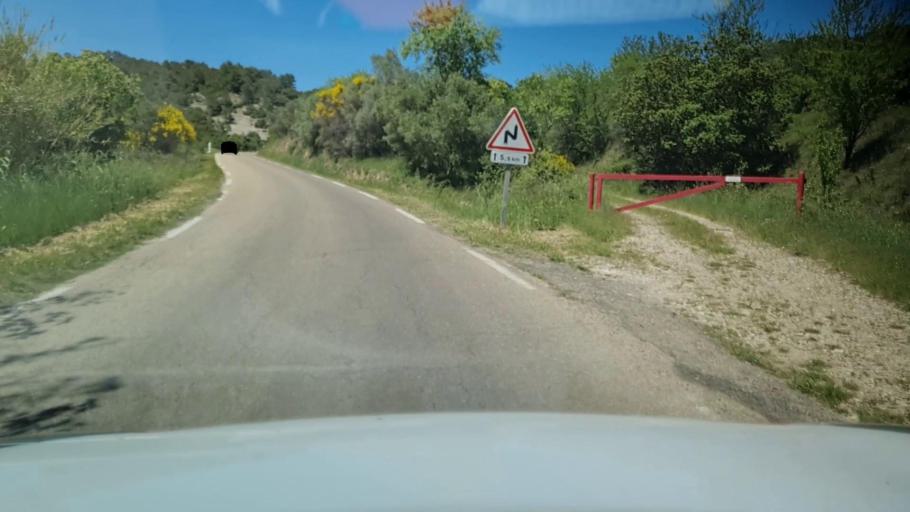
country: FR
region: Languedoc-Roussillon
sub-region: Departement du Gard
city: Clarensac
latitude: 43.8345
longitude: 4.2172
